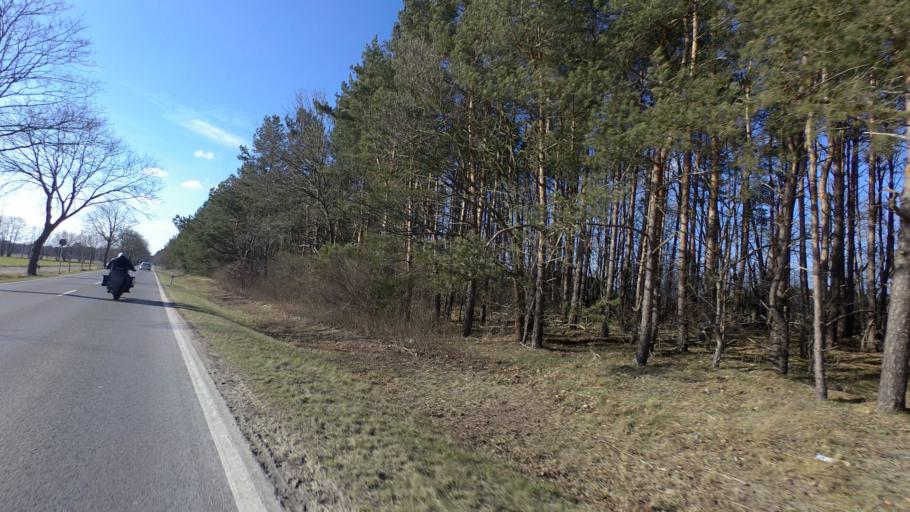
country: DE
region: Brandenburg
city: Birkenwerder
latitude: 52.7583
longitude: 13.3463
